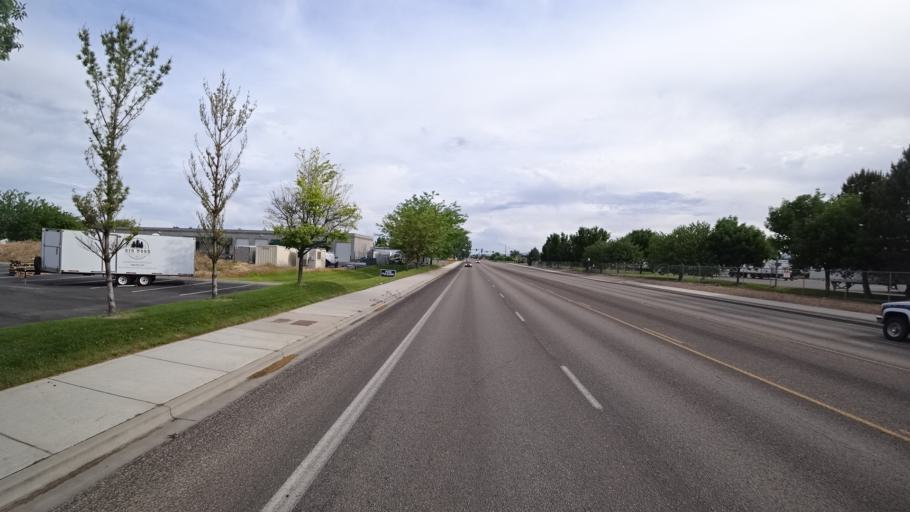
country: US
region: Idaho
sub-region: Ada County
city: Meridian
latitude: 43.6102
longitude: -116.3746
